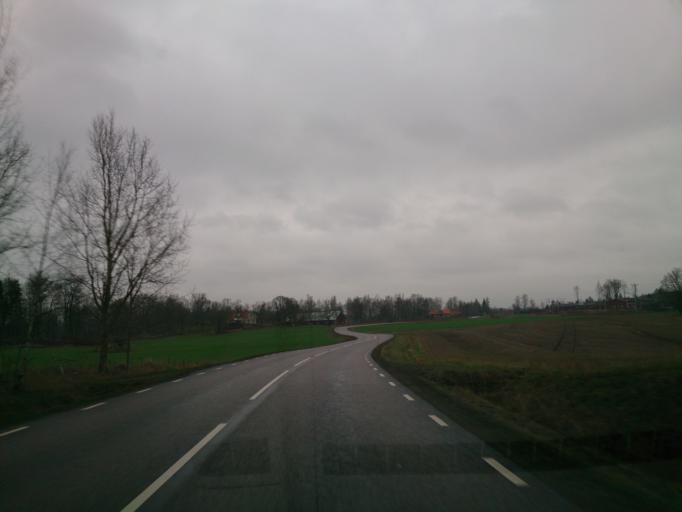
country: SE
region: OEstergoetland
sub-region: Linkopings Kommun
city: Linghem
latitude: 58.4127
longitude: 15.7623
